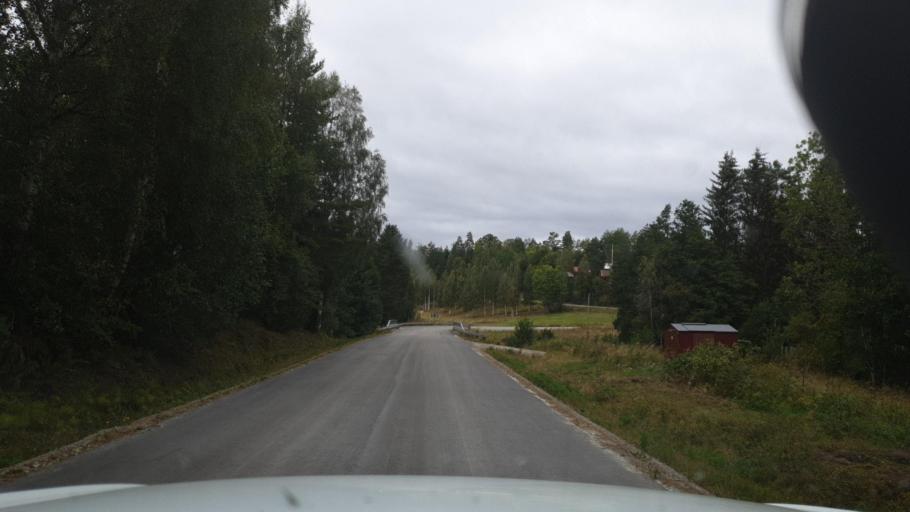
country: SE
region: Vaermland
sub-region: Sunne Kommun
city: Sunne
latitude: 59.7016
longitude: 12.8857
